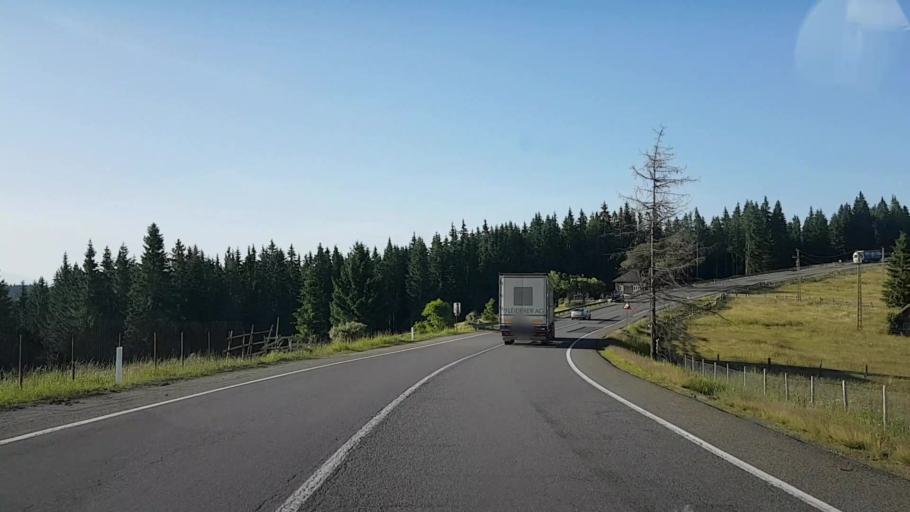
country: RO
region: Bistrita-Nasaud
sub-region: Comuna Lunca Ilvei
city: Lunca Ilvei
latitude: 47.2770
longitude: 25.0283
